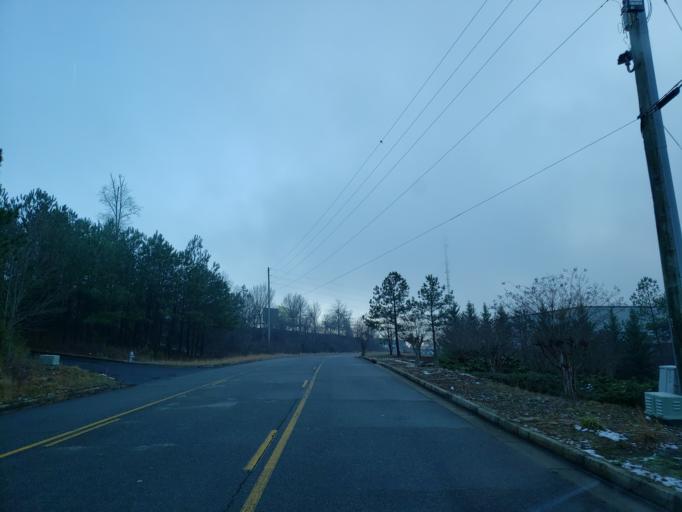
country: US
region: Georgia
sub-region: Cobb County
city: Marietta
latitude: 33.9858
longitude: -84.5644
